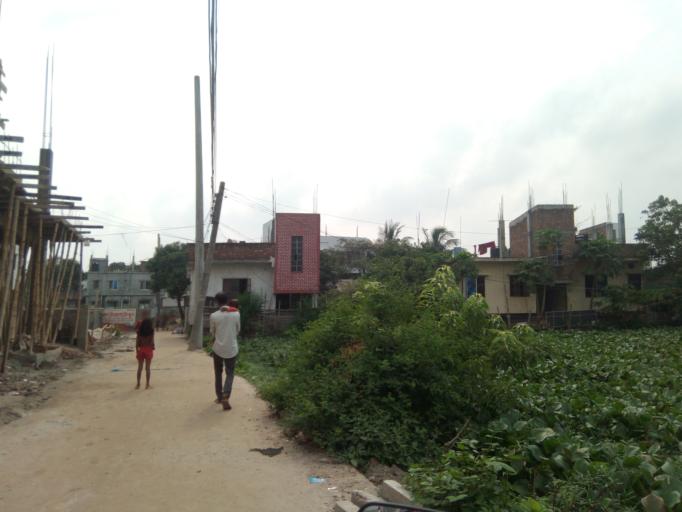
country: BD
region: Dhaka
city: Paltan
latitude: 23.7432
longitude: 90.4517
